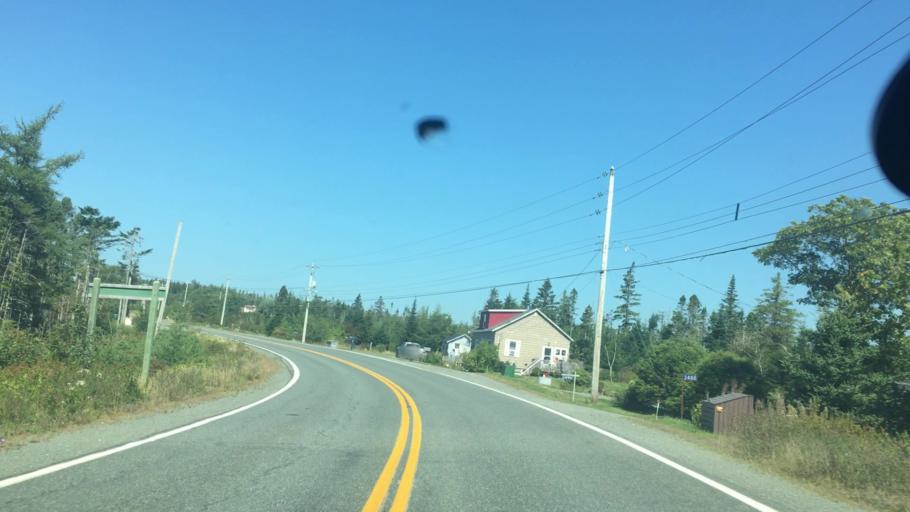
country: CA
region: Nova Scotia
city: Antigonish
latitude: 45.0001
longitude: -62.0995
